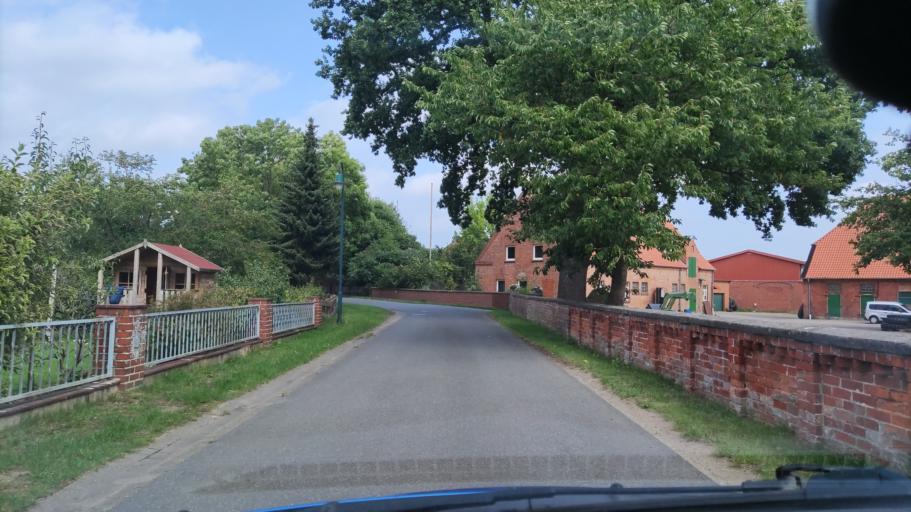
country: DE
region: Lower Saxony
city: Jelmstorf
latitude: 53.1444
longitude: 10.5358
